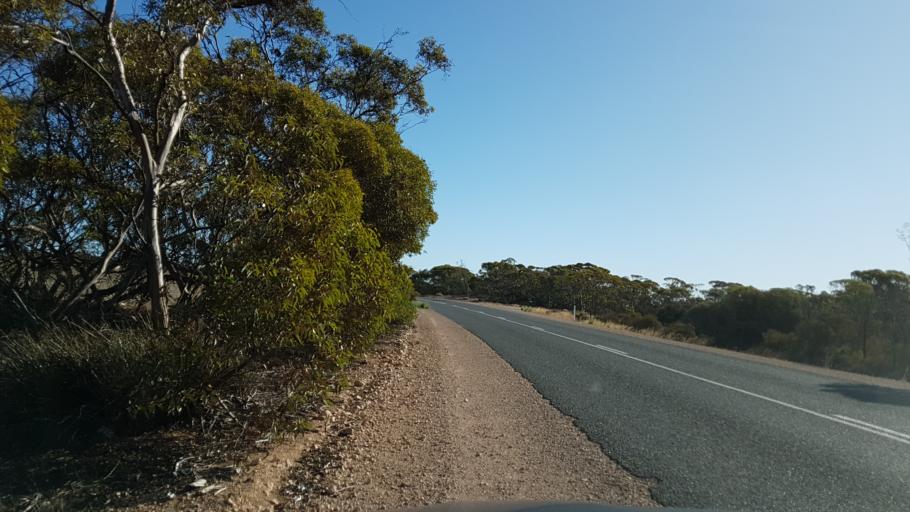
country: AU
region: South Australia
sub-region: Mid Murray
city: Mannum
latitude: -34.7956
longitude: 139.5039
